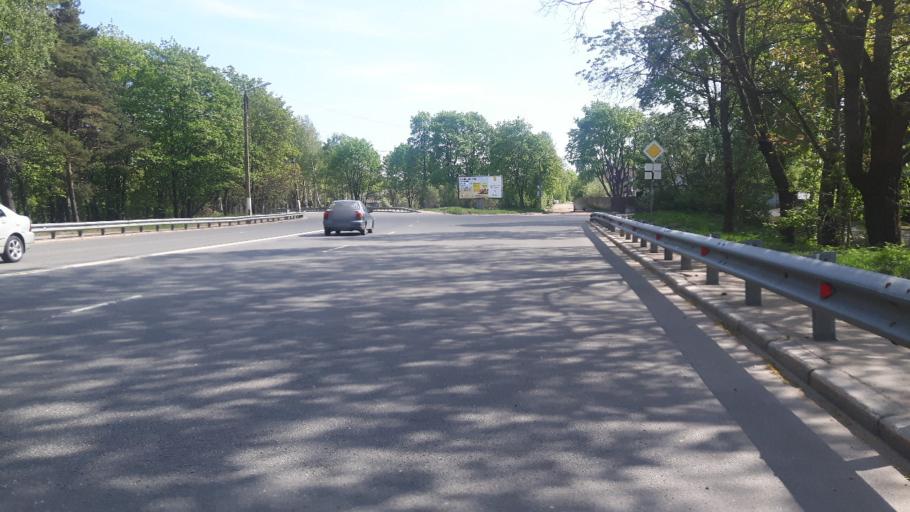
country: RU
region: Leningrad
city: Vyborg
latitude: 60.7305
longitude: 28.6988
